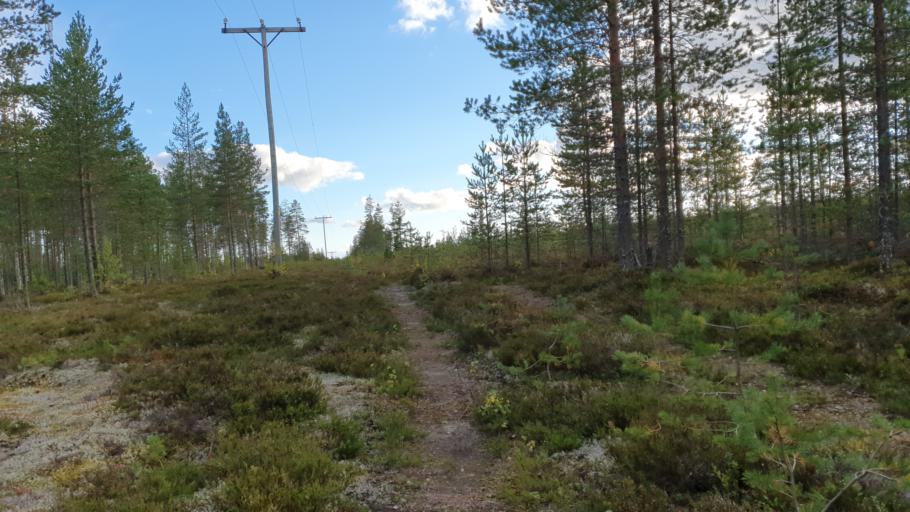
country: FI
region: Kainuu
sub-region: Kehys-Kainuu
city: Kuhmo
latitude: 64.1999
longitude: 29.1601
